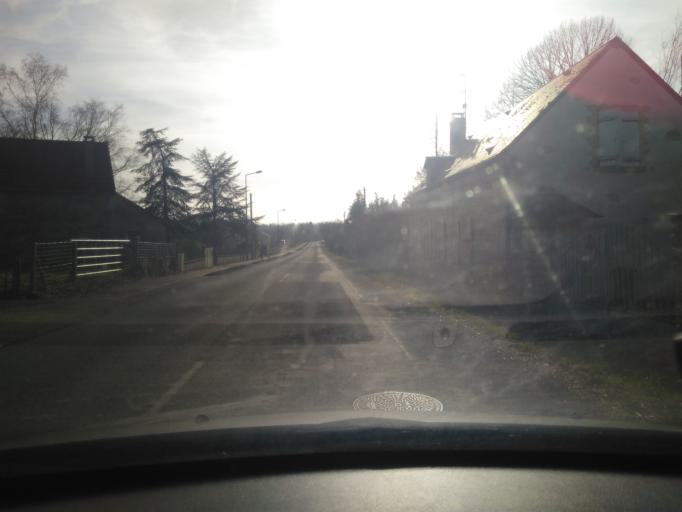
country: FR
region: Bourgogne
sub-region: Departement de la Nievre
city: Saint-Parize-le-Chatel
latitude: 46.8260
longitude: 3.2469
